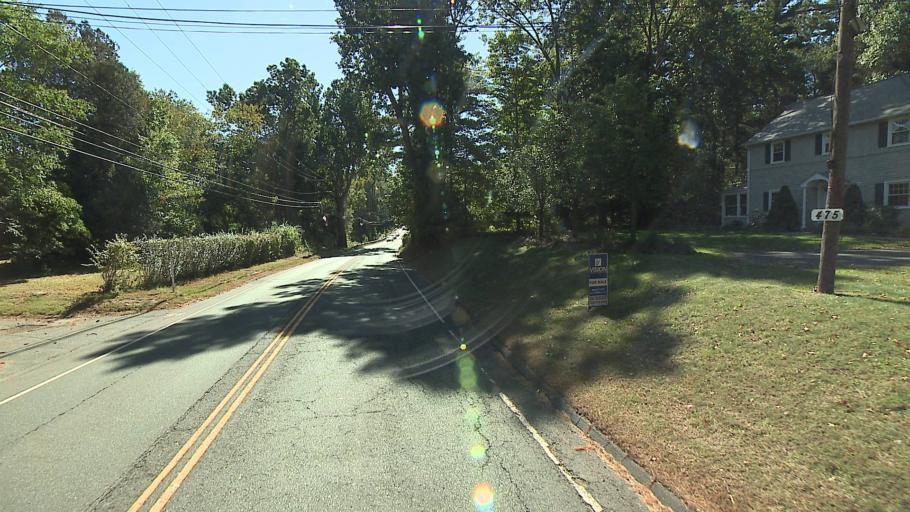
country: US
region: Connecticut
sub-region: Hartford County
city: Weatogue
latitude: 41.8572
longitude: -72.8112
